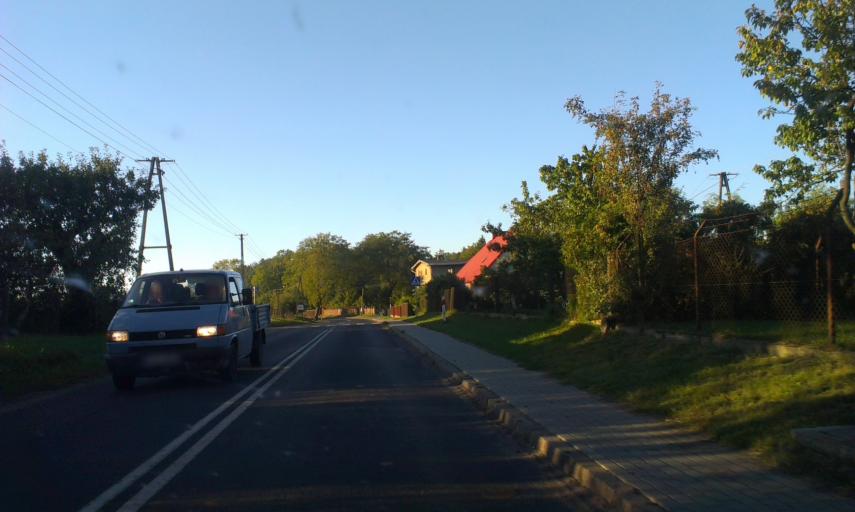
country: PL
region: Pomeranian Voivodeship
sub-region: Powiat czluchowski
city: Rzeczenica
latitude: 53.6468
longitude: 17.1456
